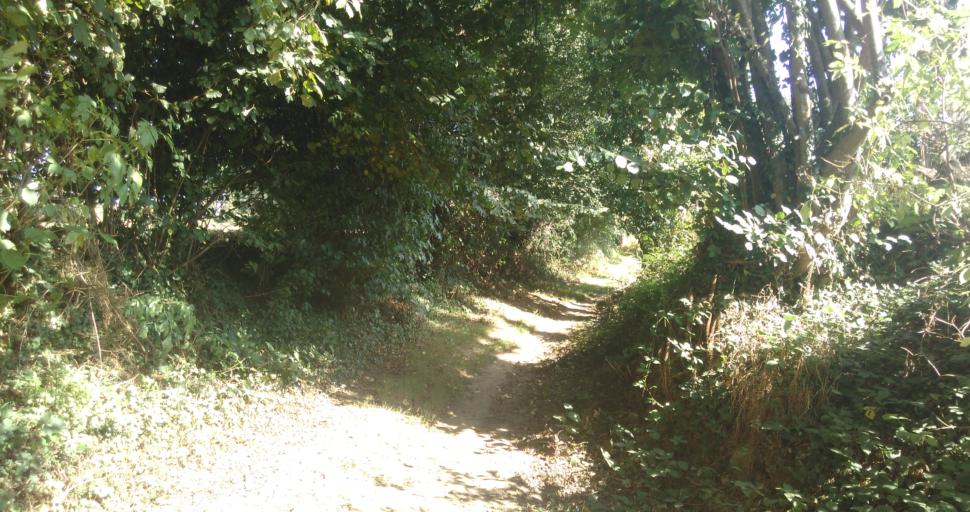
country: FR
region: Brittany
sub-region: Departement d'Ille-et-Vilaine
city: Geveze
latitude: 48.2229
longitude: -1.7785
